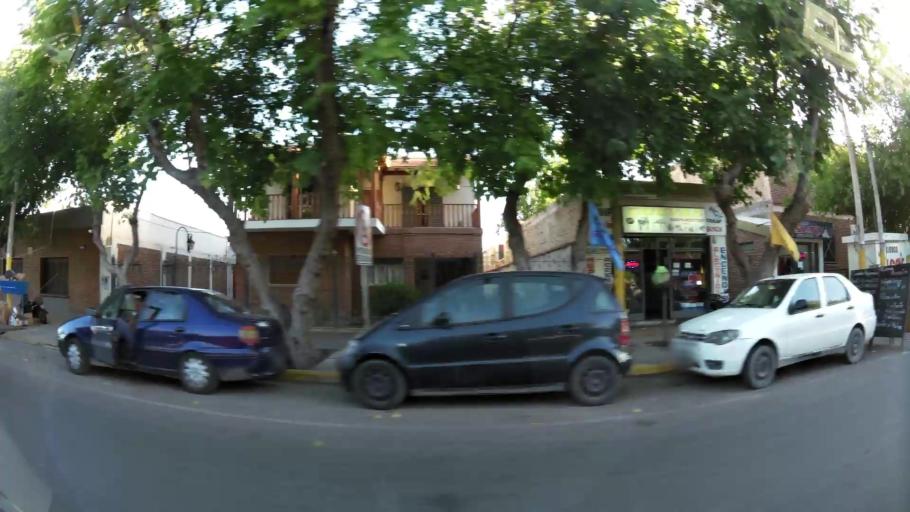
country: AR
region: San Juan
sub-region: Departamento de Santa Lucia
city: Santa Lucia
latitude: -31.5415
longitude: -68.4951
